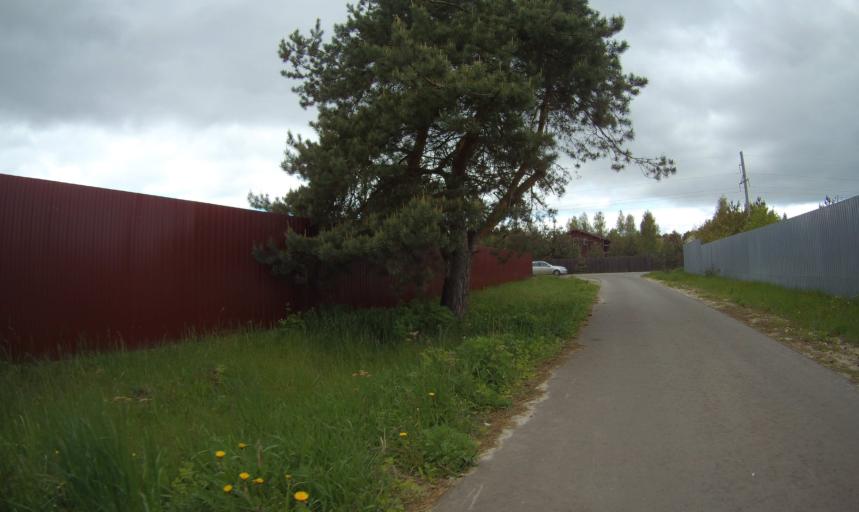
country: RU
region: Moskovskaya
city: Rechitsy
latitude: 55.5424
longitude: 38.4370
